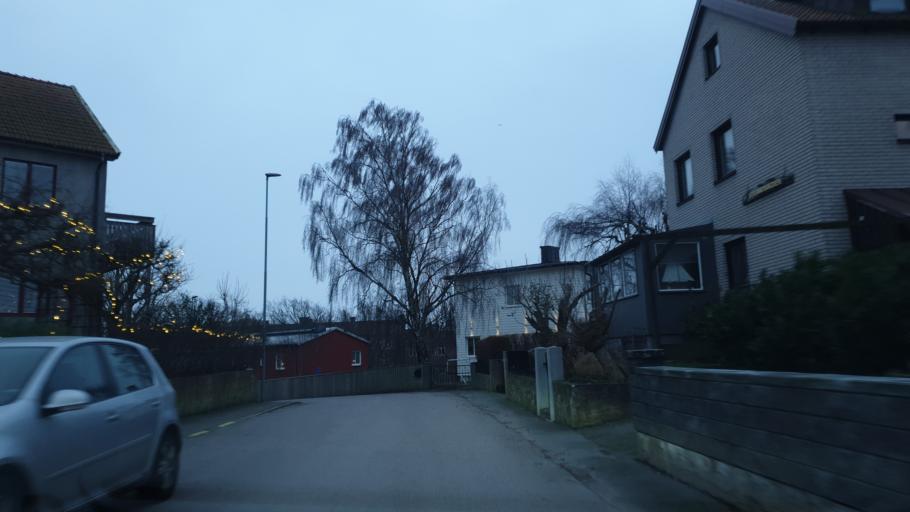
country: SE
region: Blekinge
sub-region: Karlskrona Kommun
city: Karlskrona
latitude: 56.1672
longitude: 15.5647
